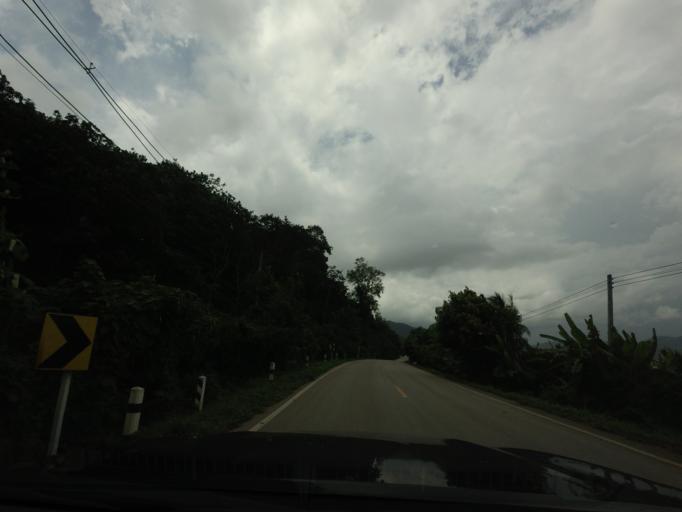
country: TH
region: Loei
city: Pak Chom
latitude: 18.0537
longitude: 101.8125
